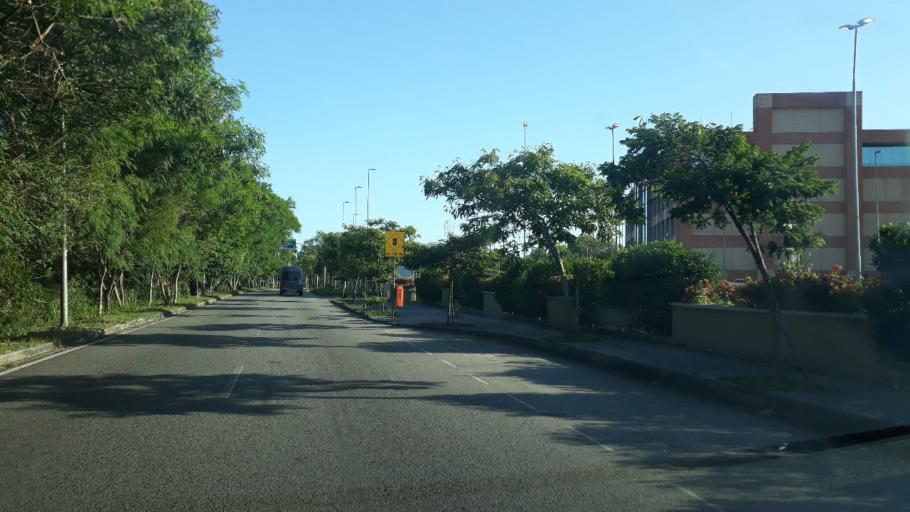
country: BR
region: Rio de Janeiro
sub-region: Rio De Janeiro
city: Rio de Janeiro
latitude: -22.9827
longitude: -43.3608
